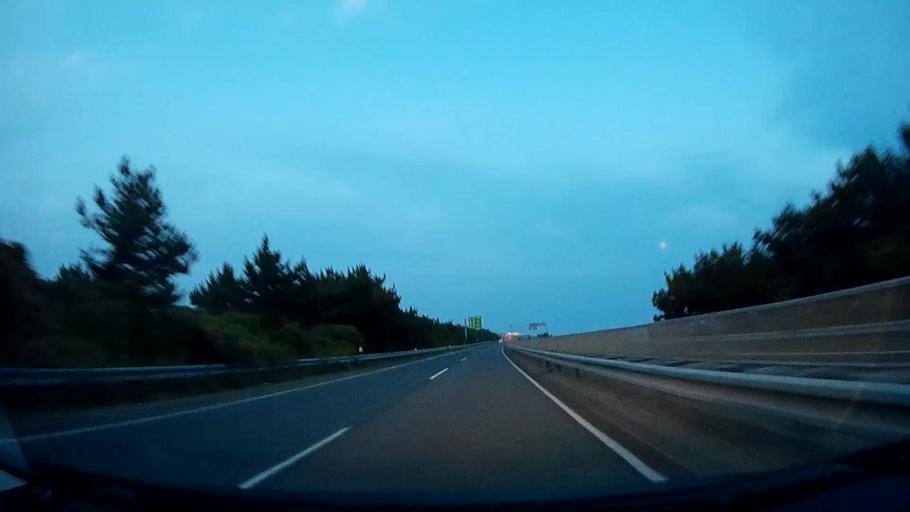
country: JP
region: Shizuoka
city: Kosai-shi
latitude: 34.6806
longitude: 137.5851
